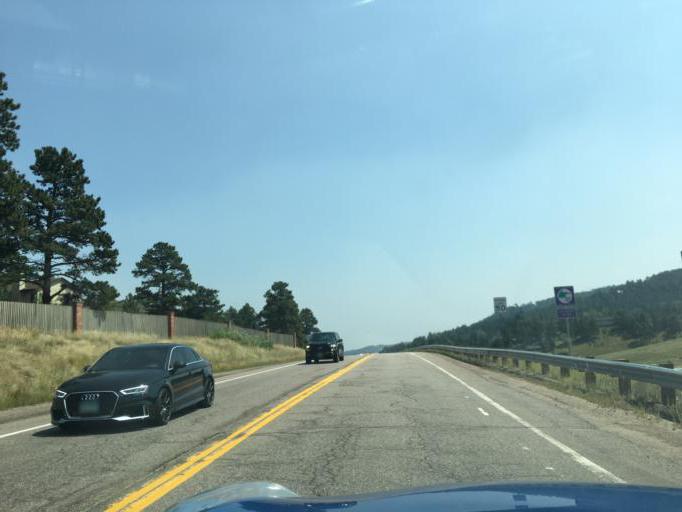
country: US
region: Colorado
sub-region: Jefferson County
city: Genesee
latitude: 39.7107
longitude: -105.2938
